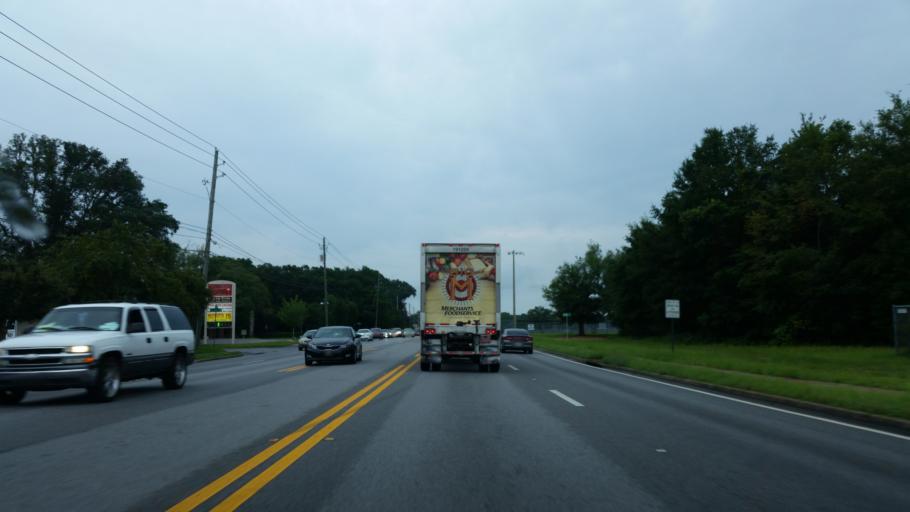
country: US
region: Florida
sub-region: Escambia County
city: Brent
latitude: 30.4629
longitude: -87.2526
